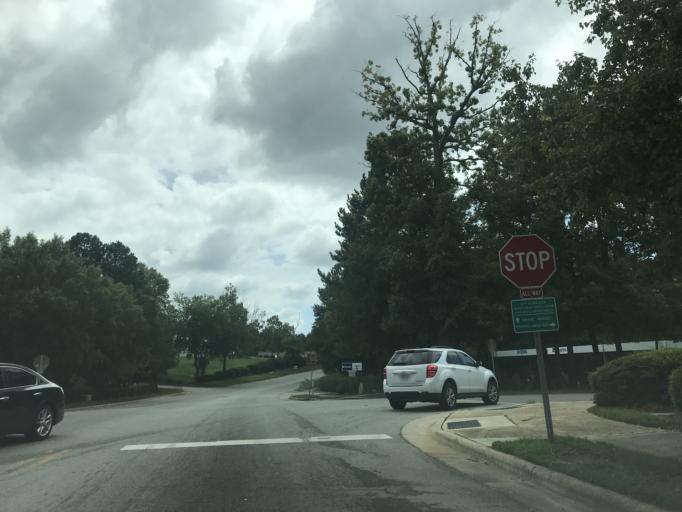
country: US
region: North Carolina
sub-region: Wake County
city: Raleigh
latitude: 35.7932
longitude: -78.5691
